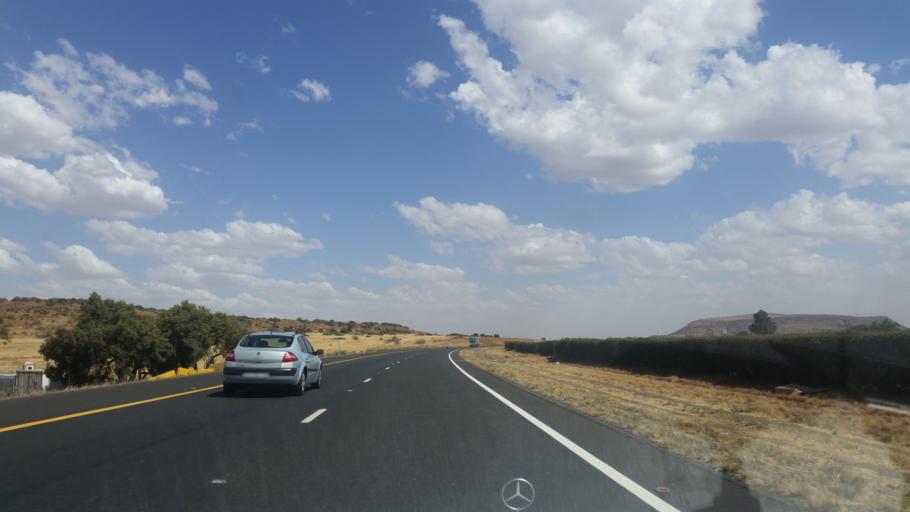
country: ZA
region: Orange Free State
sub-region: Mangaung Metropolitan Municipality
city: Bloemfontein
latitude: -29.1899
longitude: 26.1935
